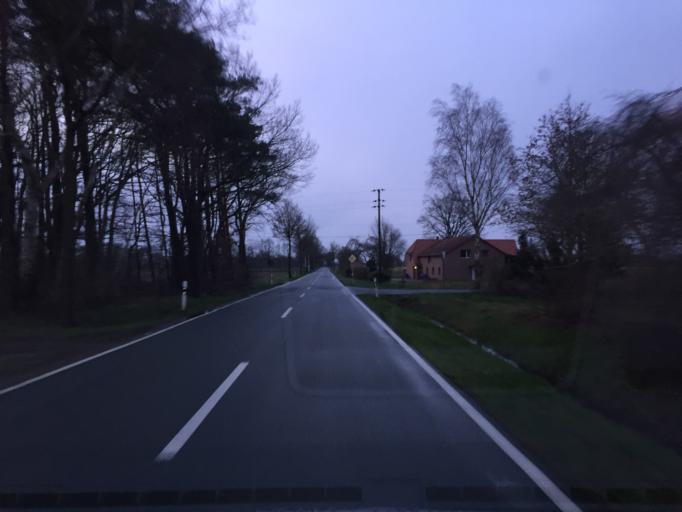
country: DE
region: Lower Saxony
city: Maasen
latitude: 52.6787
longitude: 8.8901
